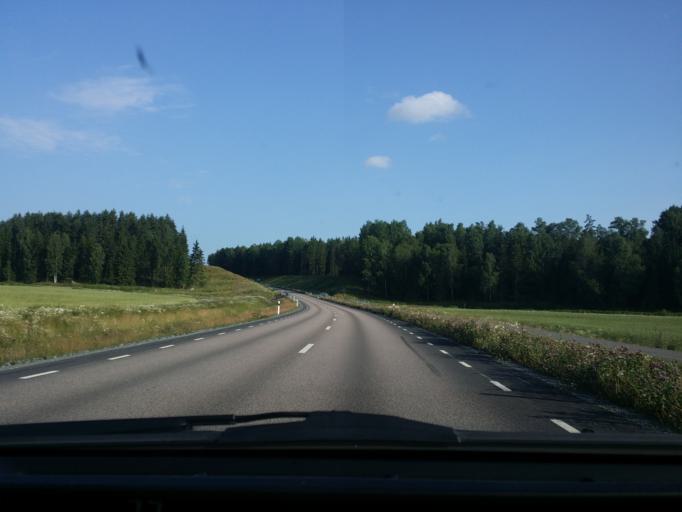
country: SE
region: Vaestmanland
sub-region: Vasteras
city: Tillberga
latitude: 59.5813
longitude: 16.6665
